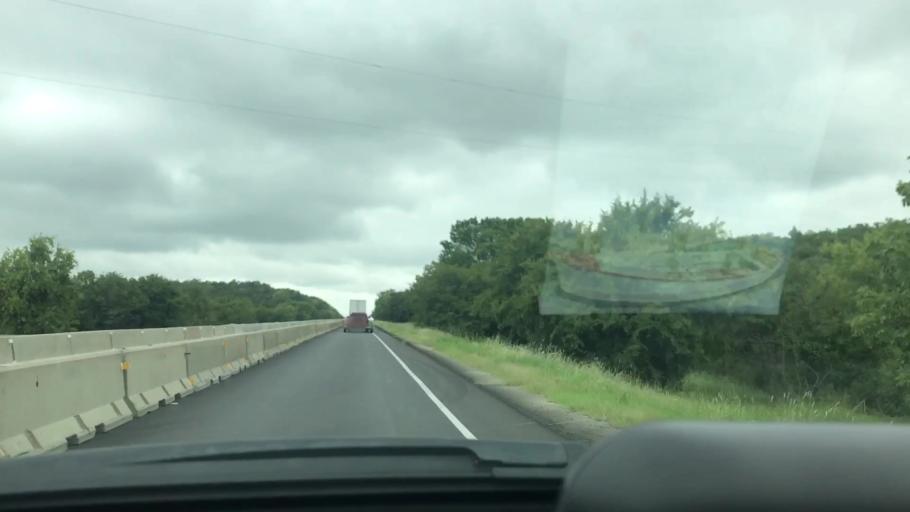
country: US
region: Oklahoma
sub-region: McIntosh County
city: Eufaula
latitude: 35.2657
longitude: -95.5903
